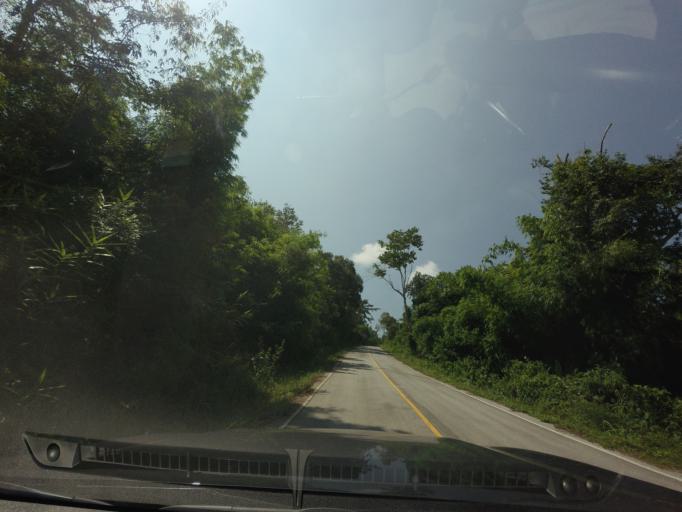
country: TH
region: Loei
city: Na Haeo
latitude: 17.5657
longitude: 100.9500
